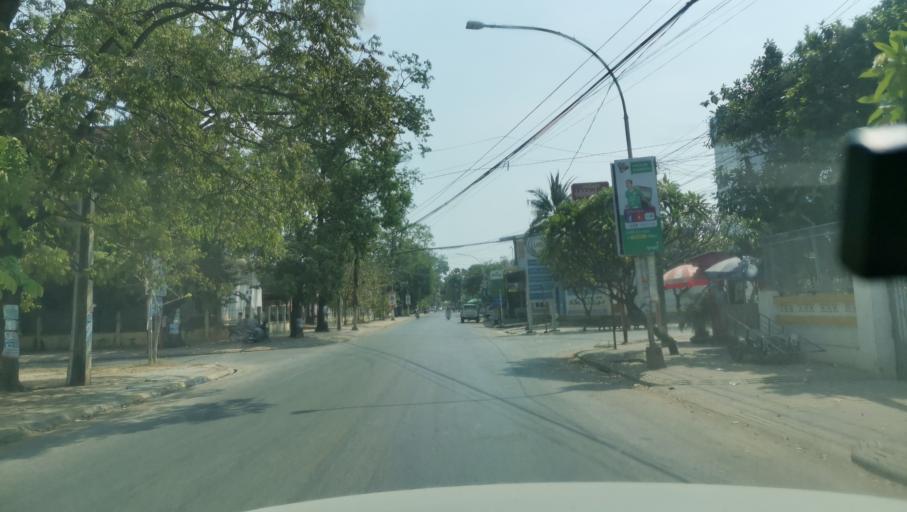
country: KH
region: Battambang
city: Battambang
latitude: 13.0890
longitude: 103.1977
